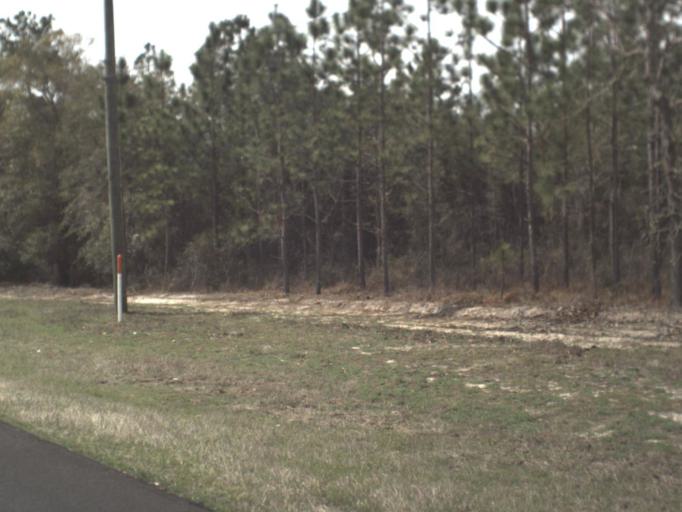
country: US
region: Florida
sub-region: Gadsden County
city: Midway
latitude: 30.4392
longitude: -84.4916
